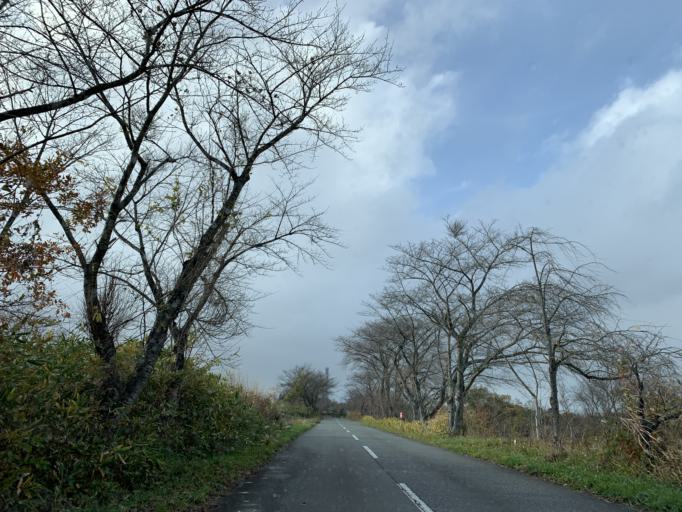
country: JP
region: Iwate
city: Mizusawa
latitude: 39.0408
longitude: 141.0787
